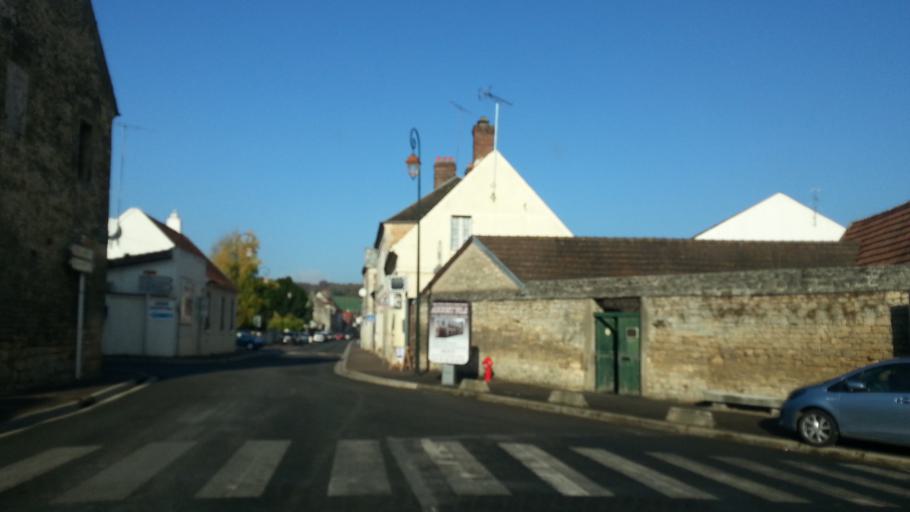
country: FR
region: Picardie
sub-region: Departement de l'Oise
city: Balagny-sur-Therain
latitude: 49.2960
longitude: 2.3359
